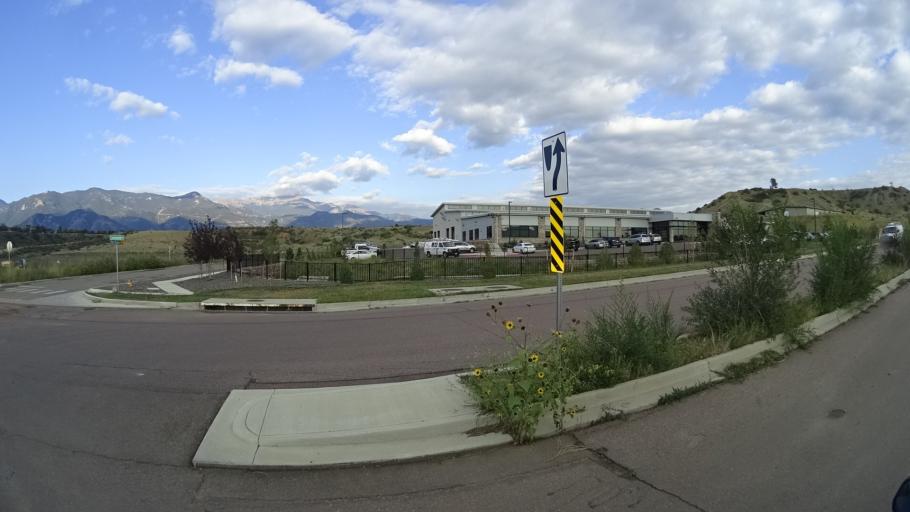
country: US
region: Colorado
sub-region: El Paso County
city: Colorado Springs
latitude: 38.8671
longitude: -104.8425
